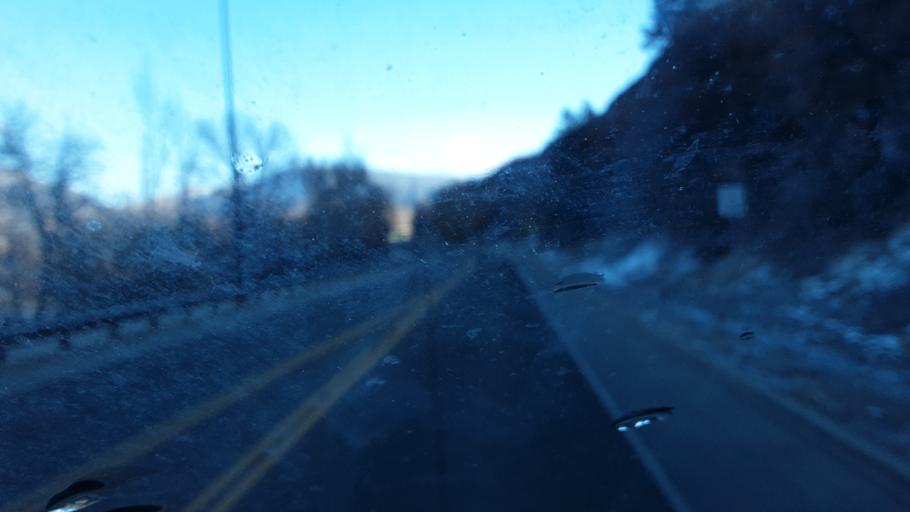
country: US
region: Colorado
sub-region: La Plata County
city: Durango
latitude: 37.2797
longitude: -107.8764
